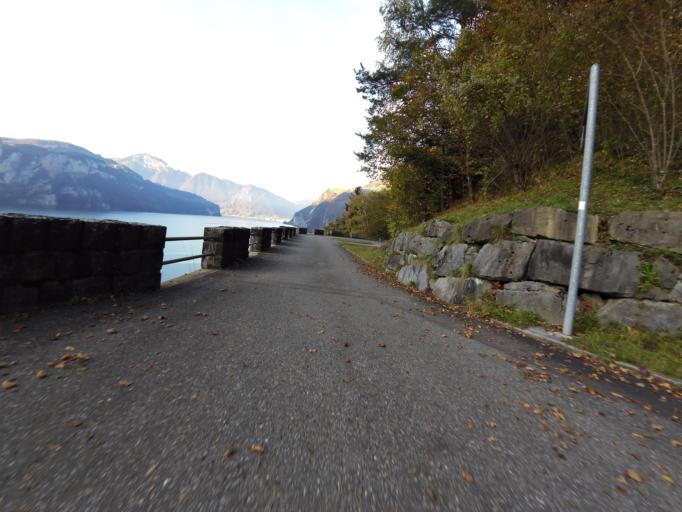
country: CH
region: Uri
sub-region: Uri
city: Flueelen
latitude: 46.9368
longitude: 8.6155
